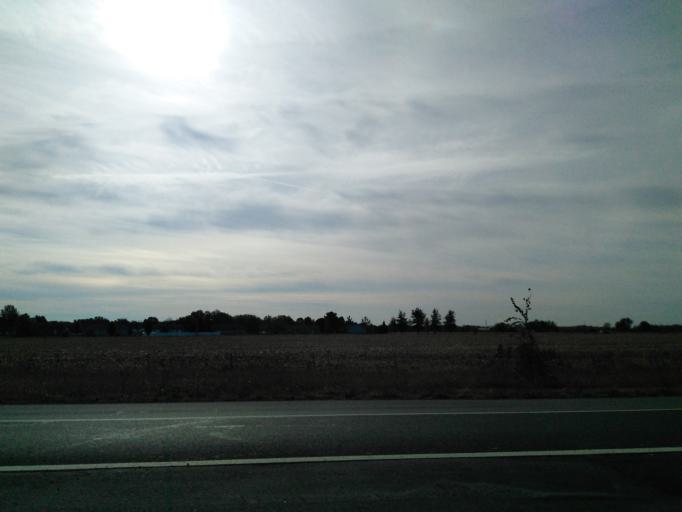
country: US
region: Illinois
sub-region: Madison County
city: Highland
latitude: 38.7863
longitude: -89.6280
